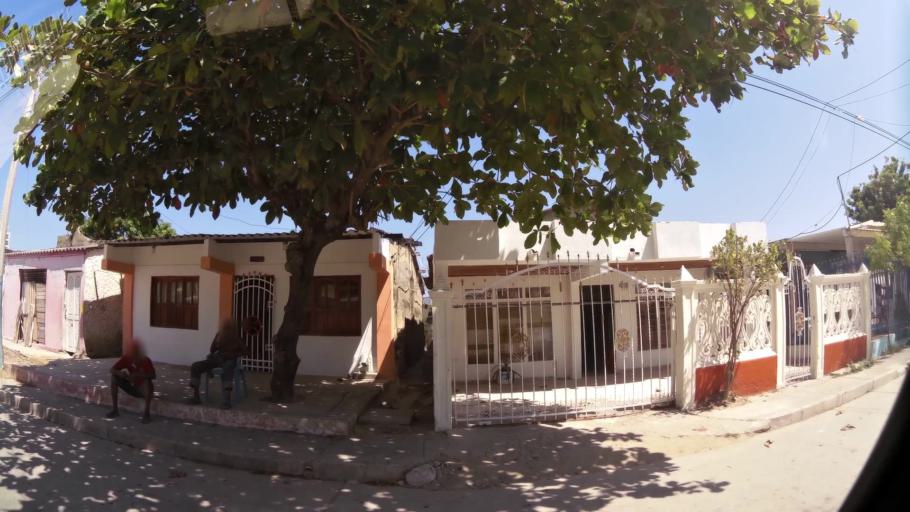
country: CO
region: Bolivar
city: Cartagena
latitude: 10.4352
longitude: -75.5316
